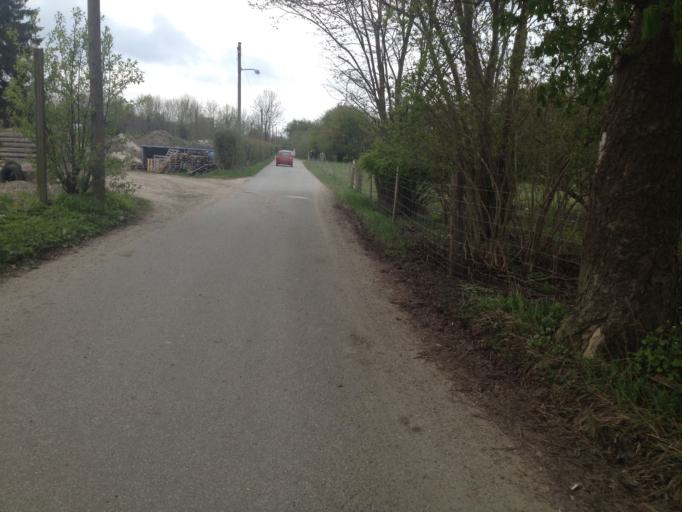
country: DK
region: Capital Region
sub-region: Ballerup Kommune
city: Ballerup
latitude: 55.7433
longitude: 12.3689
